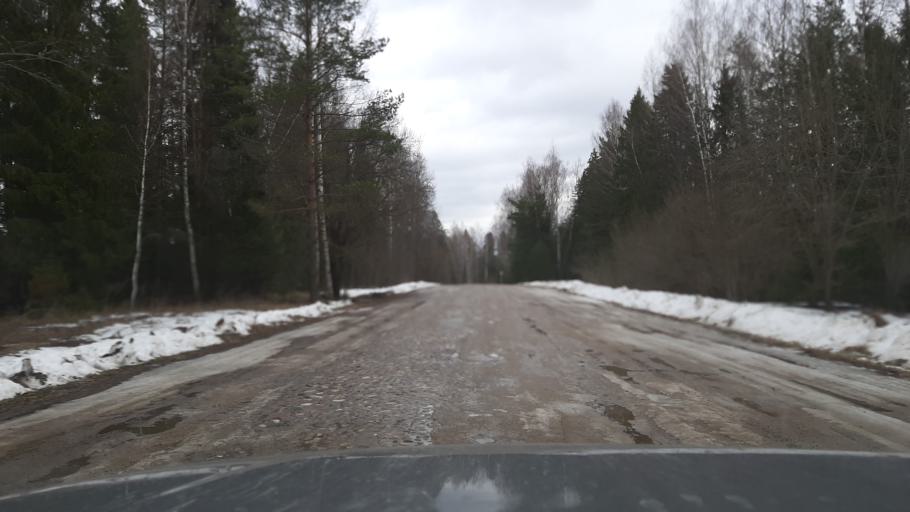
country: RU
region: Ivanovo
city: Teykovo
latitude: 56.8905
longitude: 40.6594
